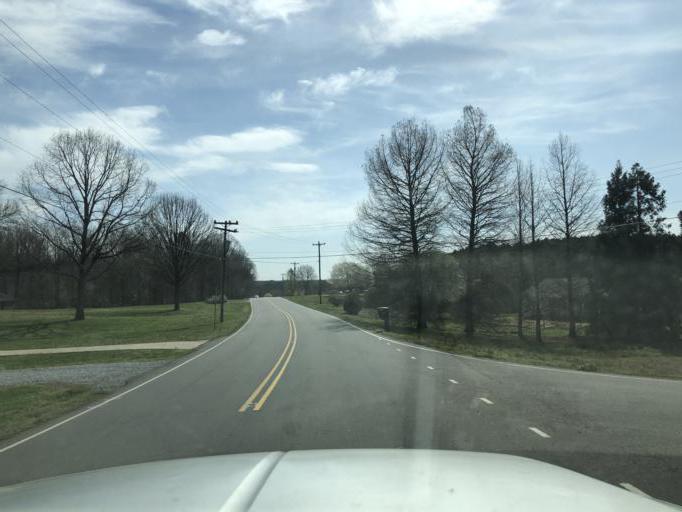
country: US
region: North Carolina
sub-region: Cleveland County
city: Shelby
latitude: 35.3480
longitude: -81.5653
